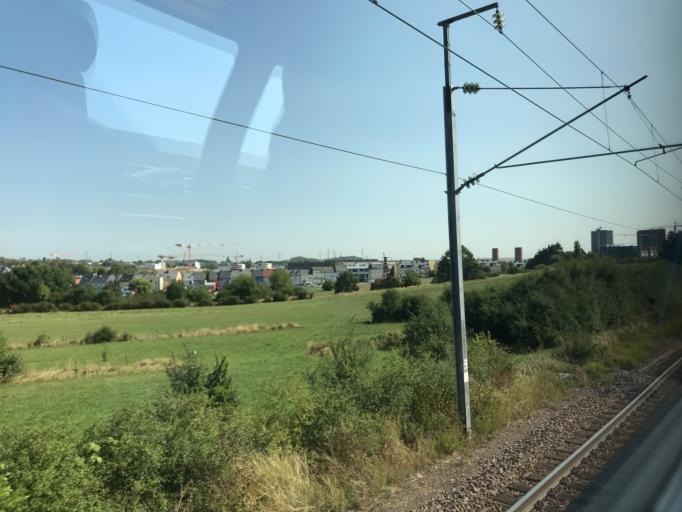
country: LU
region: Luxembourg
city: Belvaux
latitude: 49.5015
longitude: 5.9277
